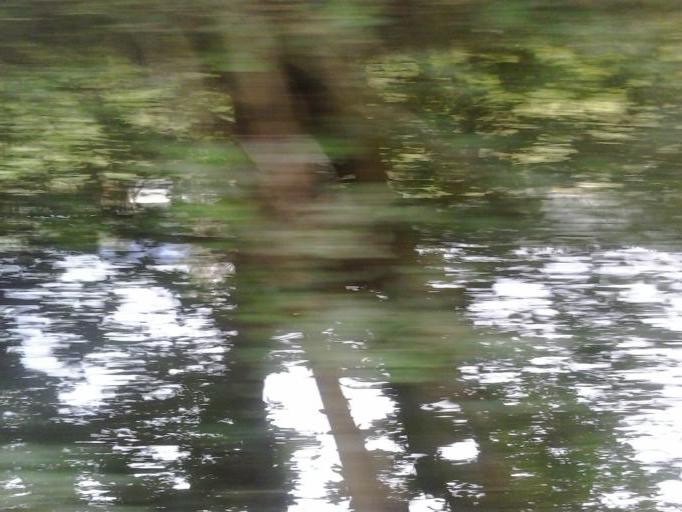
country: BR
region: Rio Grande do Sul
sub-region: Santa Maria
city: Santa Maria
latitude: -29.7226
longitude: -53.7225
